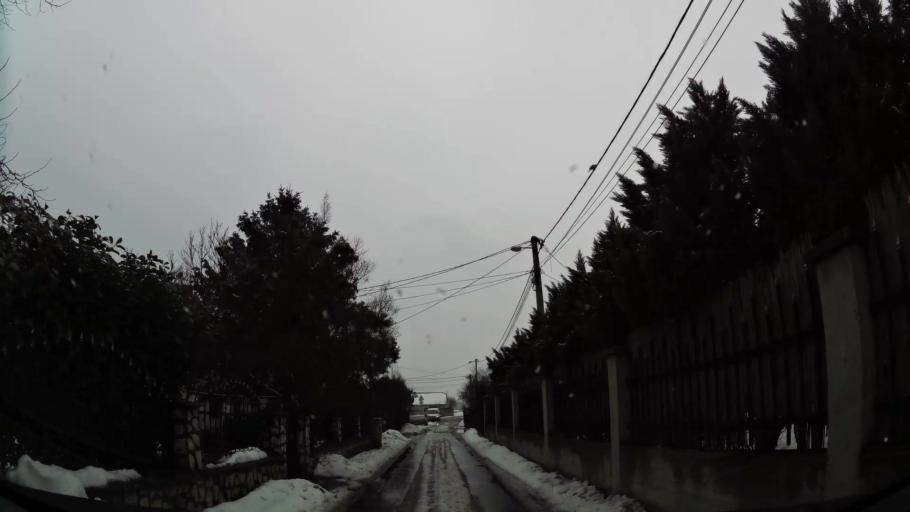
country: RS
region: Central Serbia
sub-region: Belgrade
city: Zemun
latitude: 44.8419
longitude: 20.3612
